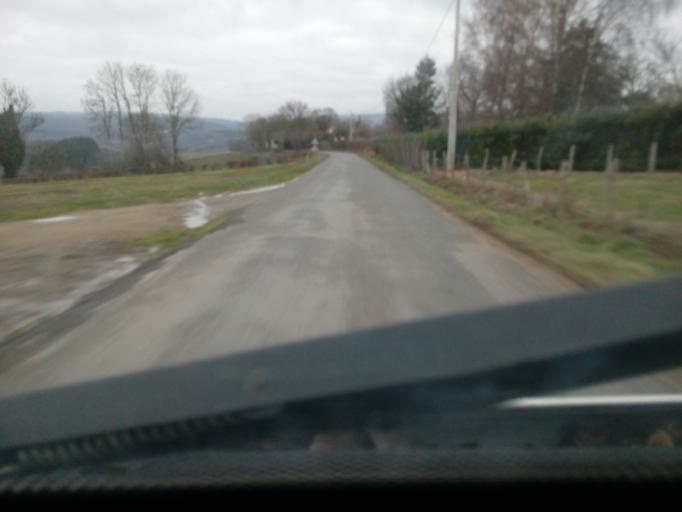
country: FR
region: Limousin
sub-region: Departement de la Creuse
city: Felletin
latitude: 45.8756
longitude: 2.1940
